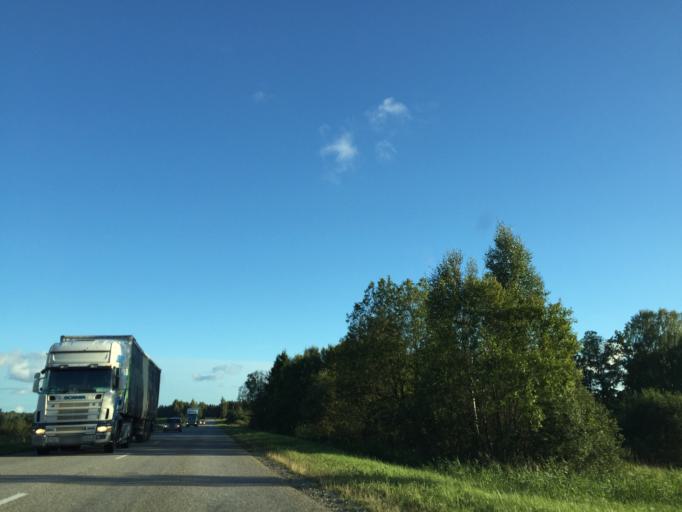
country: LV
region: Kuldigas Rajons
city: Kuldiga
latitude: 56.9230
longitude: 22.0526
